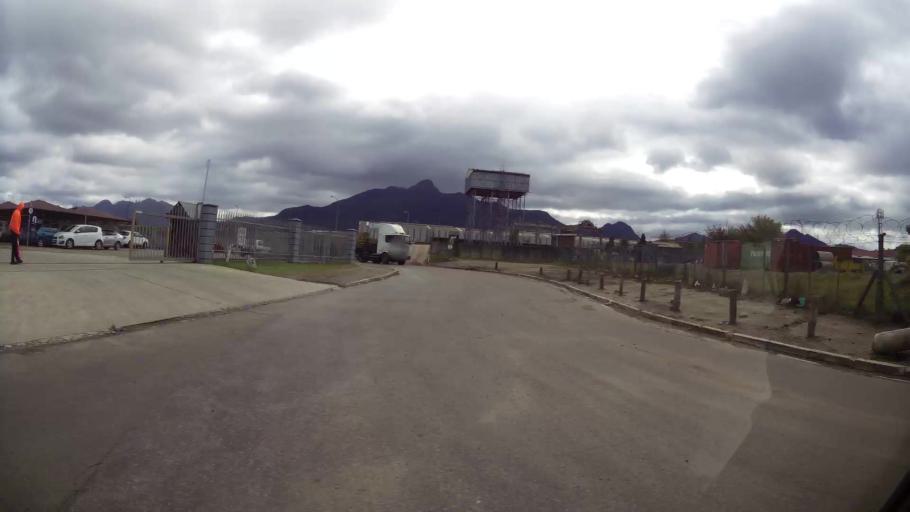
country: ZA
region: Western Cape
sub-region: Eden District Municipality
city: George
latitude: -33.9651
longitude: 22.4734
